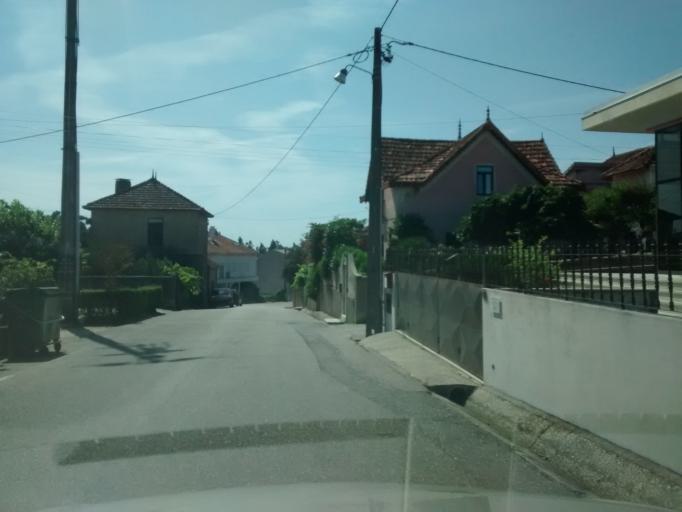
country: PT
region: Aveiro
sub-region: Mealhada
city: Pampilhosa do Botao
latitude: 40.3840
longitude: -8.3818
